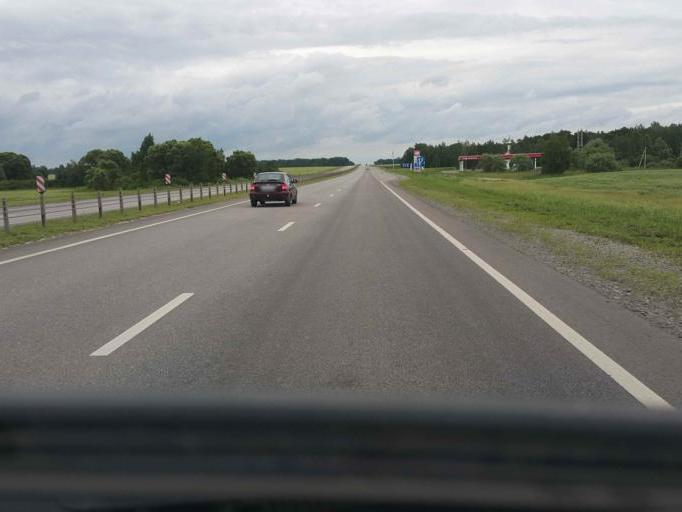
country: RU
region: Tambov
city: Zavoronezhskoye
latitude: 52.9020
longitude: 40.6563
